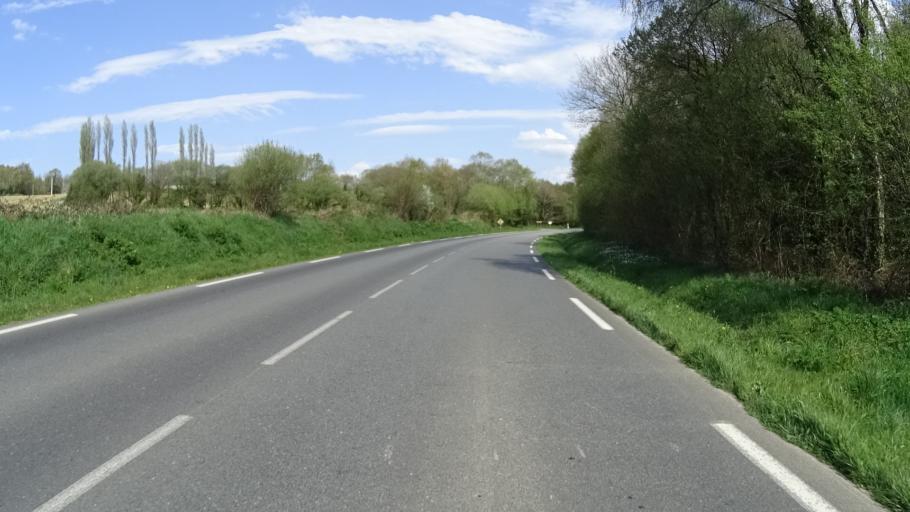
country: FR
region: Brittany
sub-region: Departement du Finistere
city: Sizun
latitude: 48.4384
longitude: -4.1010
